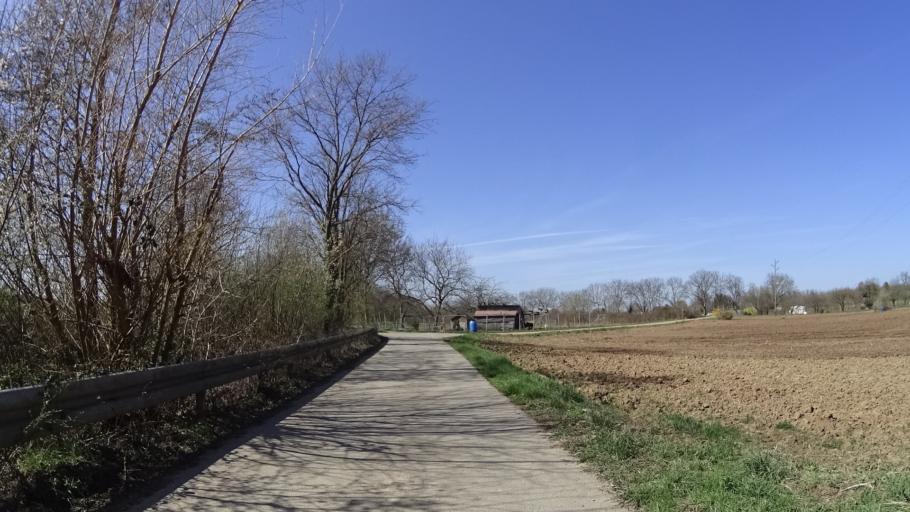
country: DE
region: Baden-Wuerttemberg
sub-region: Karlsruhe Region
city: Dossenheim
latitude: 49.4497
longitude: 8.6548
